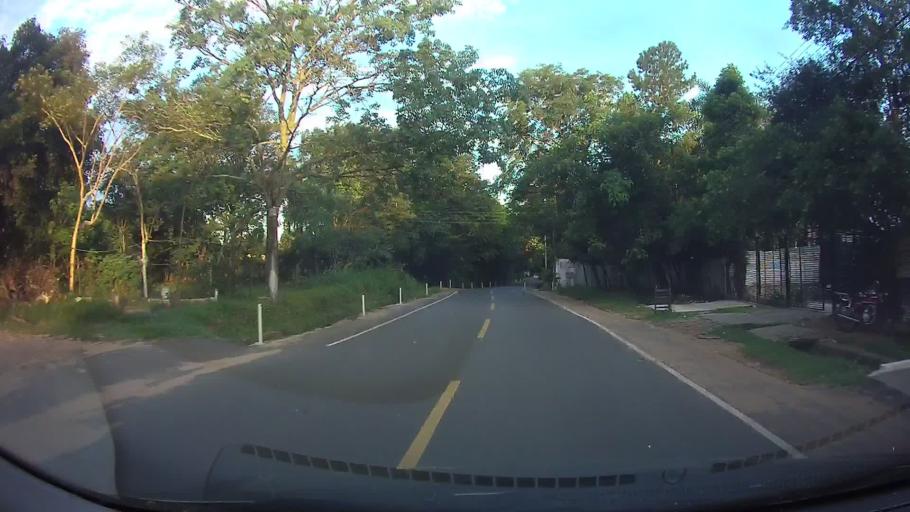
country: PY
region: Central
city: Limpio
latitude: -25.2504
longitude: -57.5013
